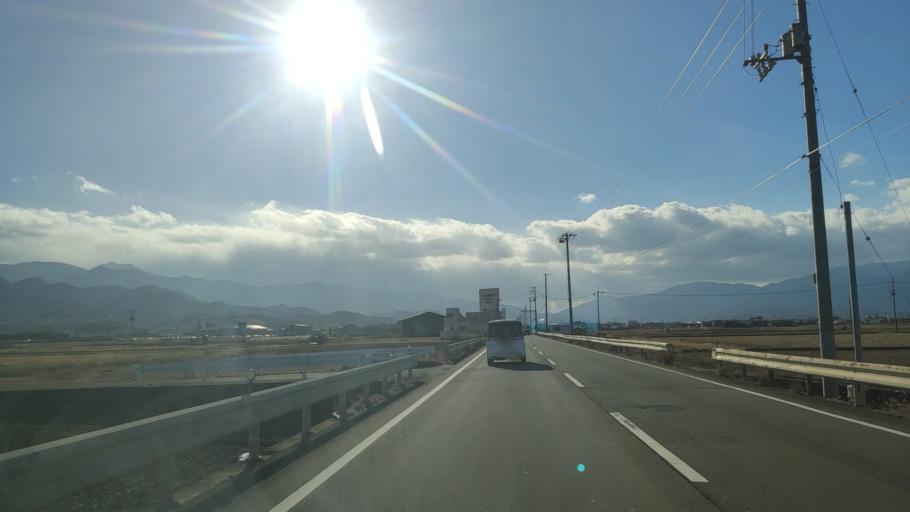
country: JP
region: Ehime
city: Saijo
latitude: 33.9158
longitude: 133.1196
